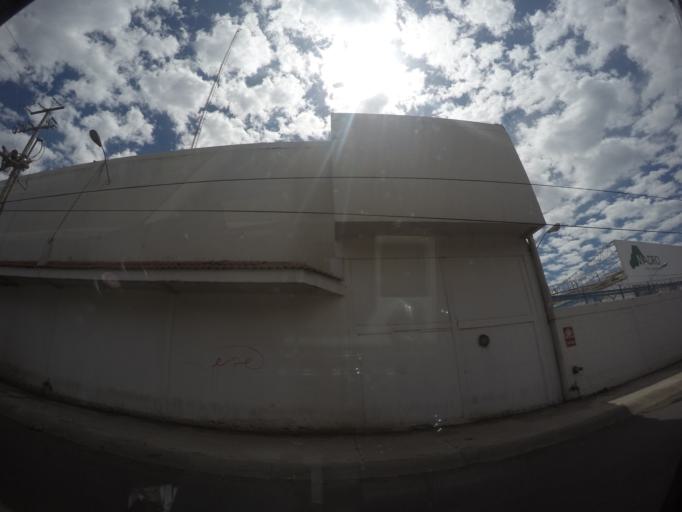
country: MX
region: Guanajuato
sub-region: Leon
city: Santa Ana
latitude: 21.0558
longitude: -101.6877
